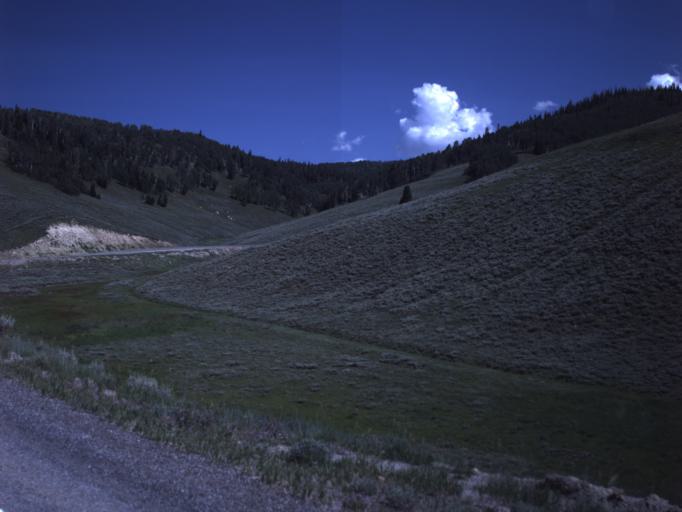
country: US
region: Utah
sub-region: Sanpete County
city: Fairview
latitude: 39.6830
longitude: -111.2453
